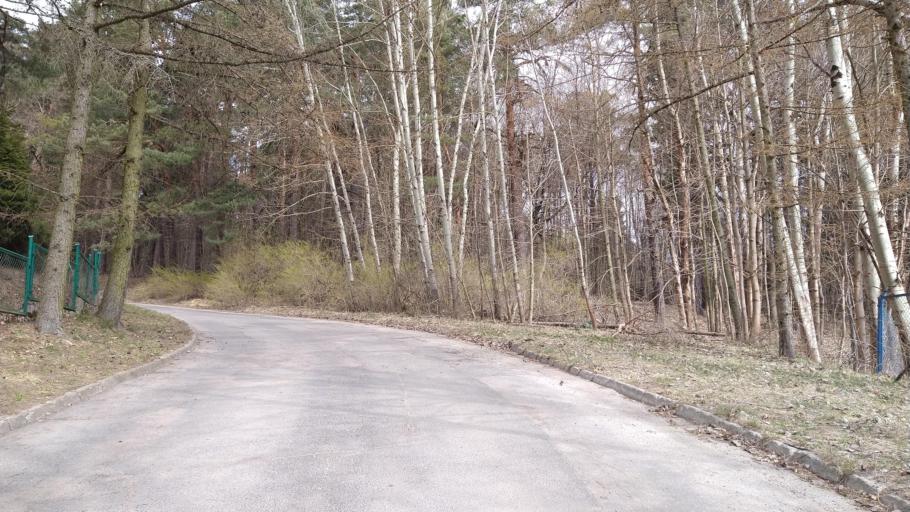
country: PL
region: Warmian-Masurian Voivodeship
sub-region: Powiat olsztynski
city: Olsztyn
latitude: 53.8021
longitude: 20.4915
